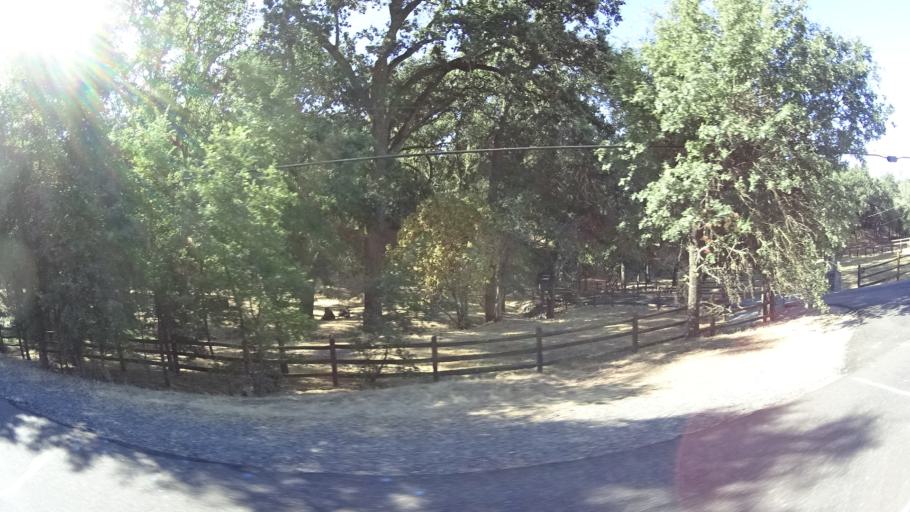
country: US
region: California
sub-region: Calaveras County
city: San Andreas
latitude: 38.2533
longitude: -120.7124
